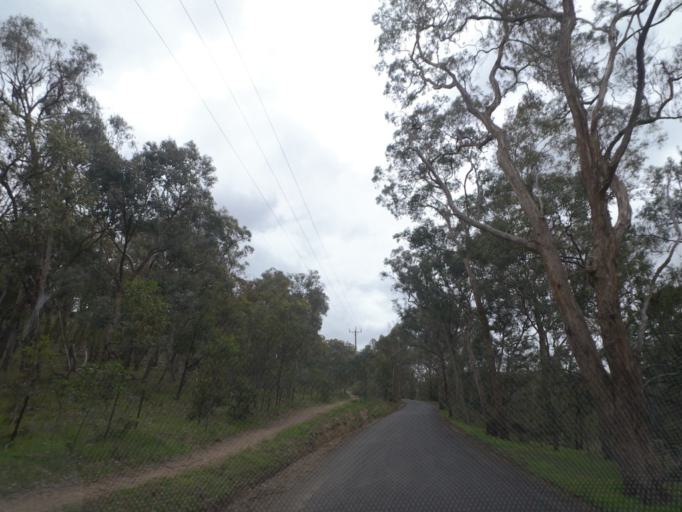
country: AU
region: Victoria
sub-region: Nillumbik
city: Wattleglen
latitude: -37.6727
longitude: 145.2277
